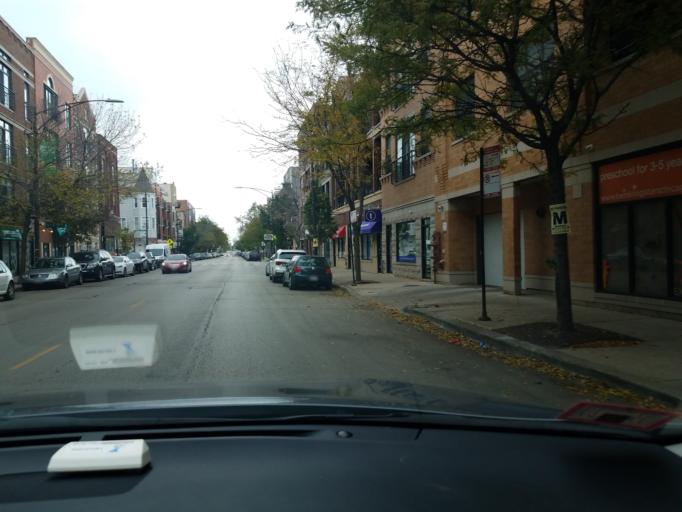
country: US
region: Illinois
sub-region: Cook County
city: Lincolnwood
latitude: 41.9396
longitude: -87.6798
